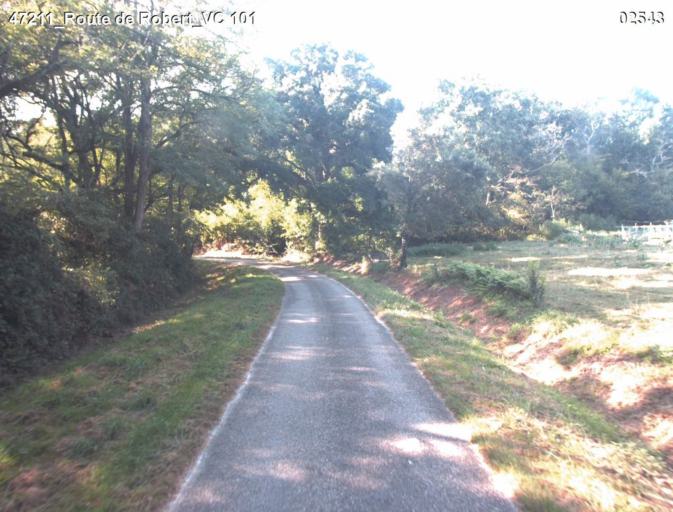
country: FR
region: Aquitaine
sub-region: Departement du Lot-et-Garonne
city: Mezin
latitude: 44.0530
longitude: 0.1808
